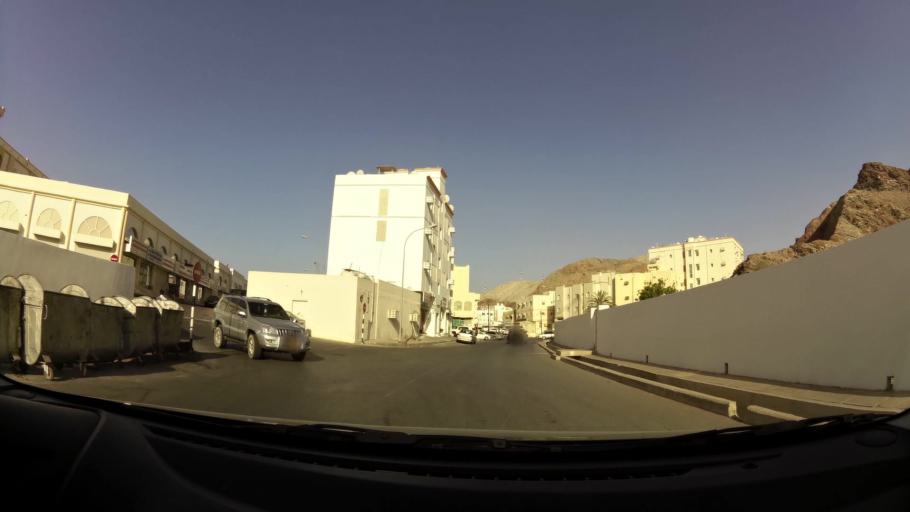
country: OM
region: Muhafazat Masqat
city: Muscat
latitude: 23.5852
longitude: 58.5440
